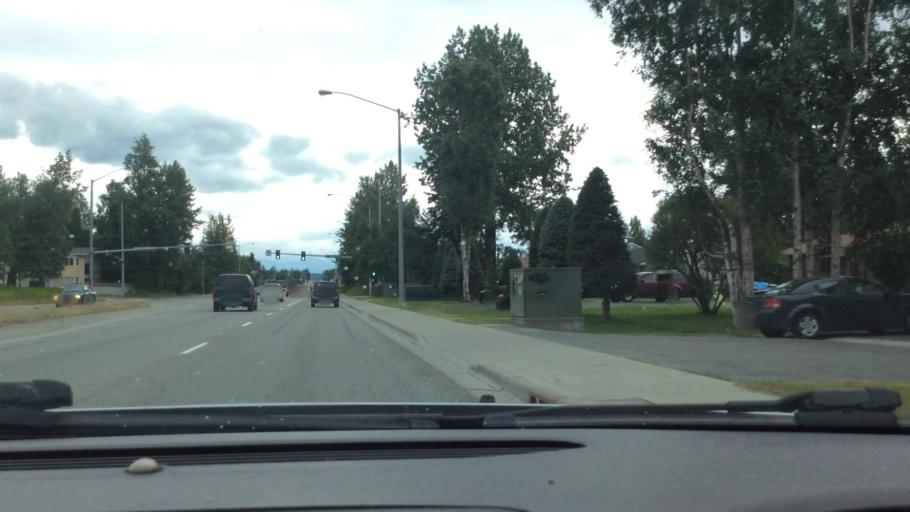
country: US
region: Alaska
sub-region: Anchorage Municipality
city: Anchorage
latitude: 61.2000
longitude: -149.7786
